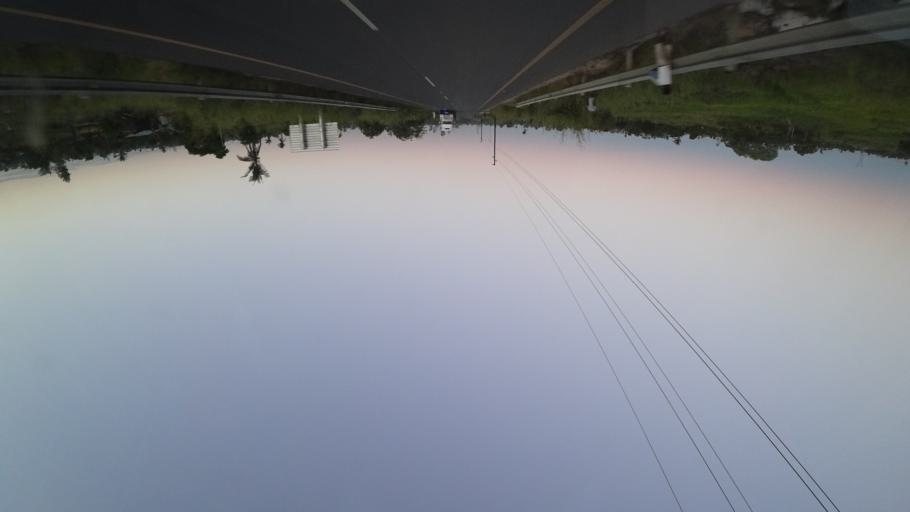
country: MZ
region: Sofala
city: Dondo
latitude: -19.5242
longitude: 34.6242
